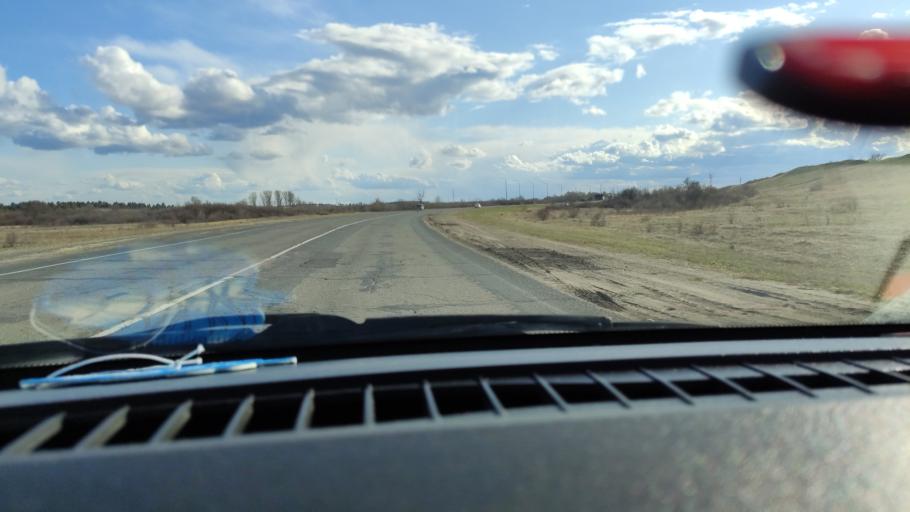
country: RU
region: Saratov
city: Sennoy
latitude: 52.0892
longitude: 46.8073
